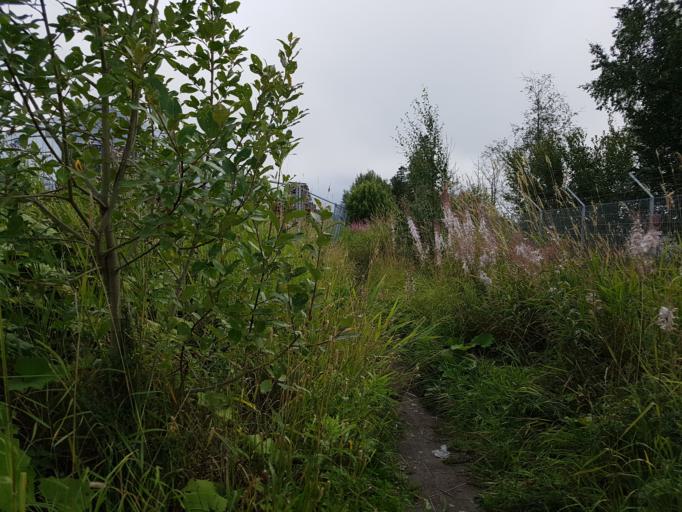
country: NO
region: Sor-Trondelag
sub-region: Trondheim
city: Trondheim
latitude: 63.4242
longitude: 10.4765
